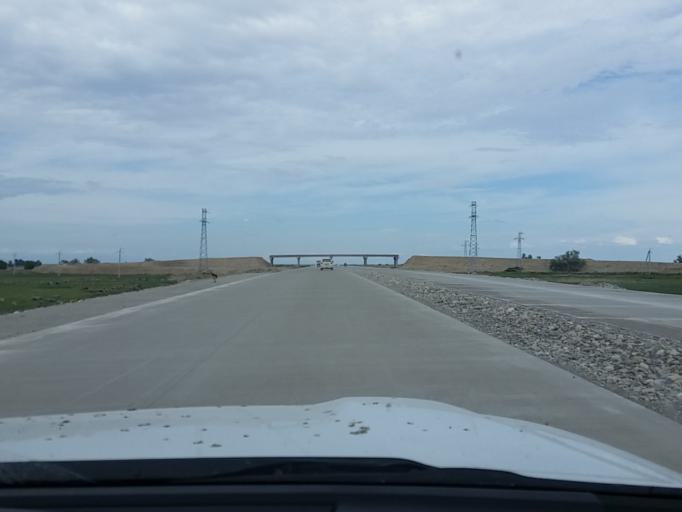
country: KZ
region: Almaty Oblysy
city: Zharkent
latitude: 44.0293
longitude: 79.9021
